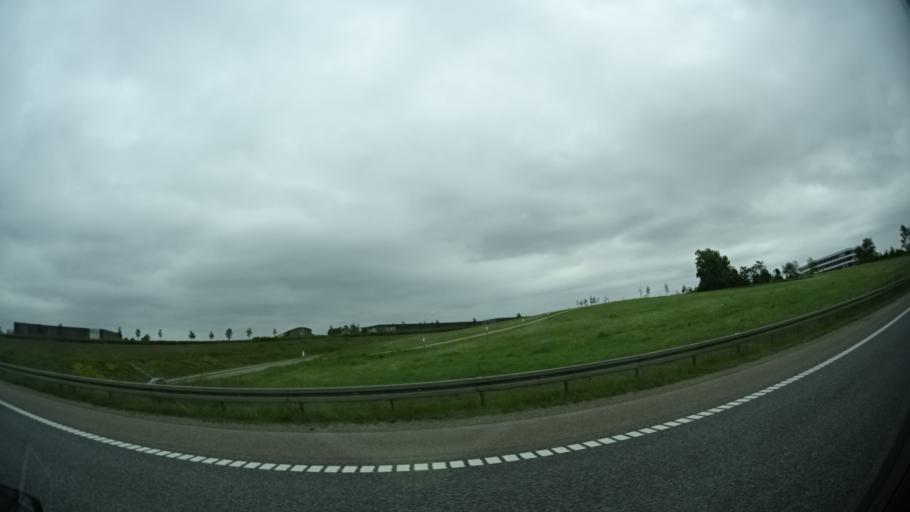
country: DK
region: Central Jutland
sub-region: Arhus Kommune
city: Trige
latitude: 56.2158
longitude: 10.1402
